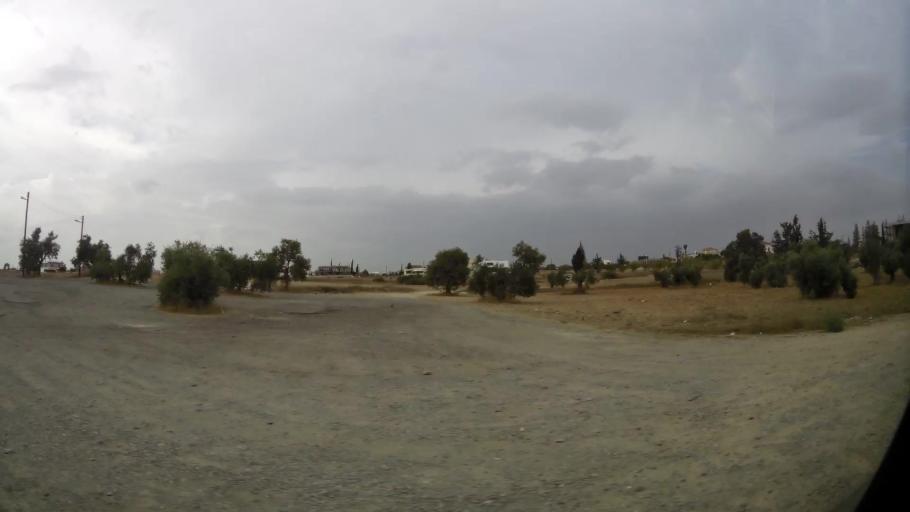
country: CY
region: Lefkosia
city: Geri
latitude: 35.0902
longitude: 33.3929
